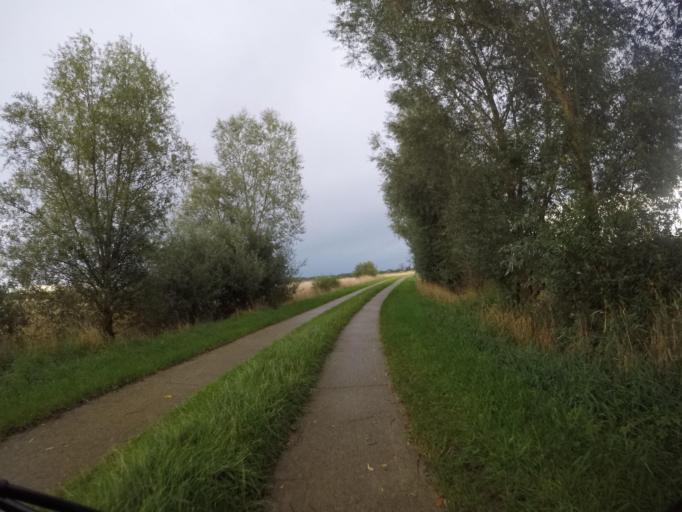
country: DE
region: Lower Saxony
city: Neu Darchau
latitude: 53.2598
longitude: 10.8964
